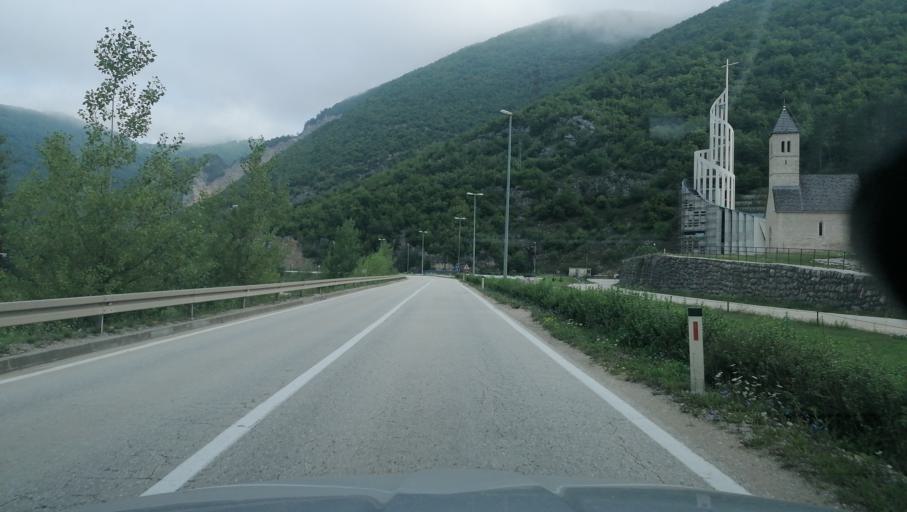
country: BA
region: Federation of Bosnia and Herzegovina
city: Divicani
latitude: 44.3745
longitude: 17.2942
